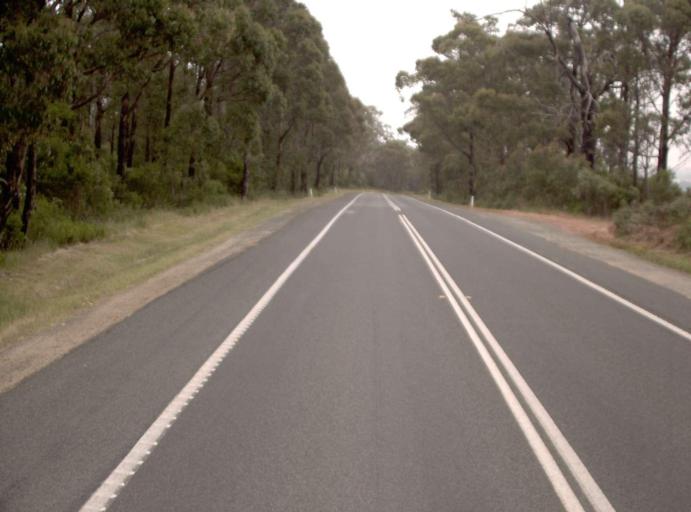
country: AU
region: Victoria
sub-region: Latrobe
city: Moe
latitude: -38.3296
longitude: 146.2539
